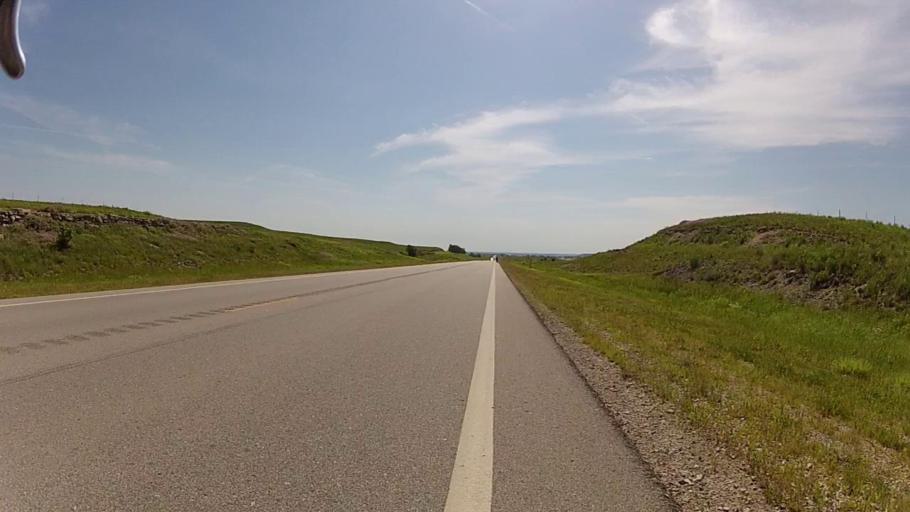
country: US
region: Kansas
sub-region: Cowley County
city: Winfield
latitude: 37.1107
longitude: -96.6368
